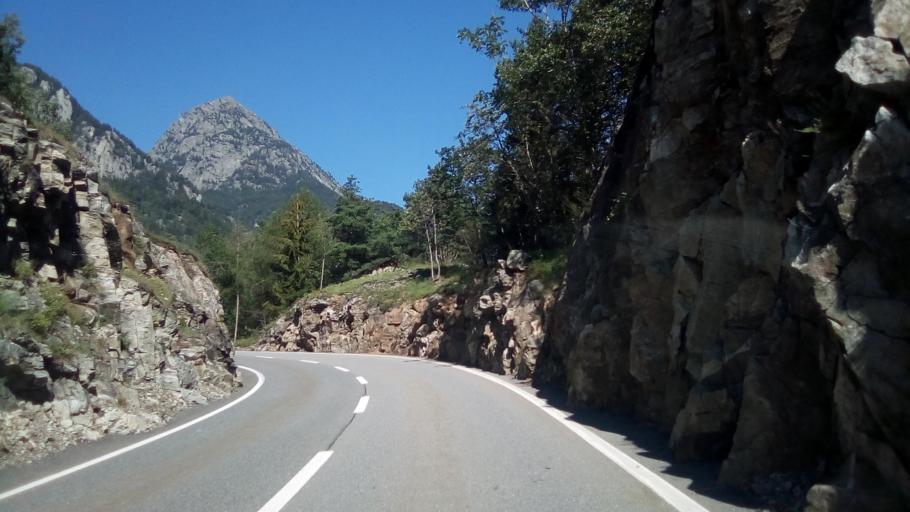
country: CH
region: Valais
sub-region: Saint-Maurice District
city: Vernayaz
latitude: 46.1282
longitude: 7.0359
